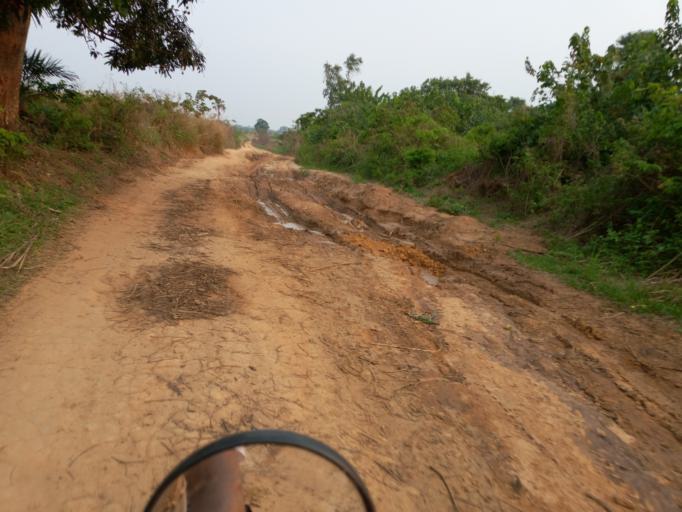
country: CD
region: Bandundu
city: Bandundu
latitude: -3.4420
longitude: 17.6053
